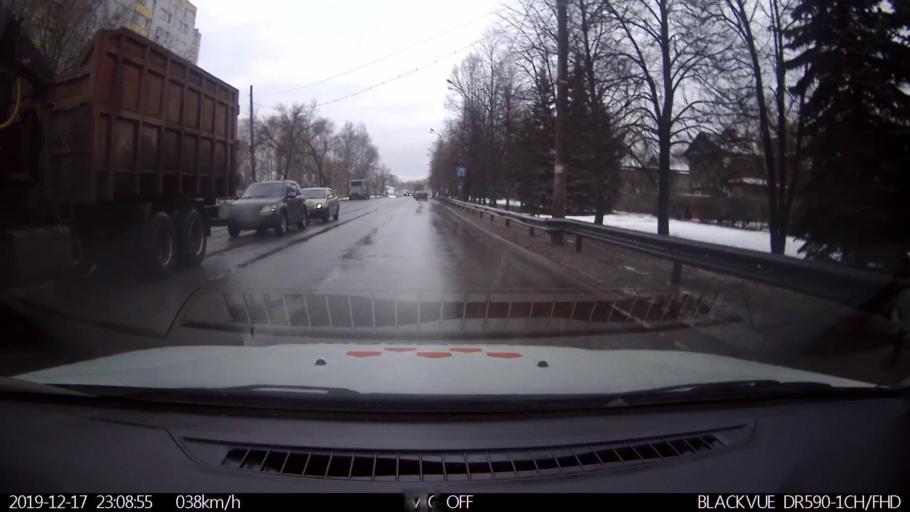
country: RU
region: Nizjnij Novgorod
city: Gorbatovka
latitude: 56.3456
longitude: 43.8395
